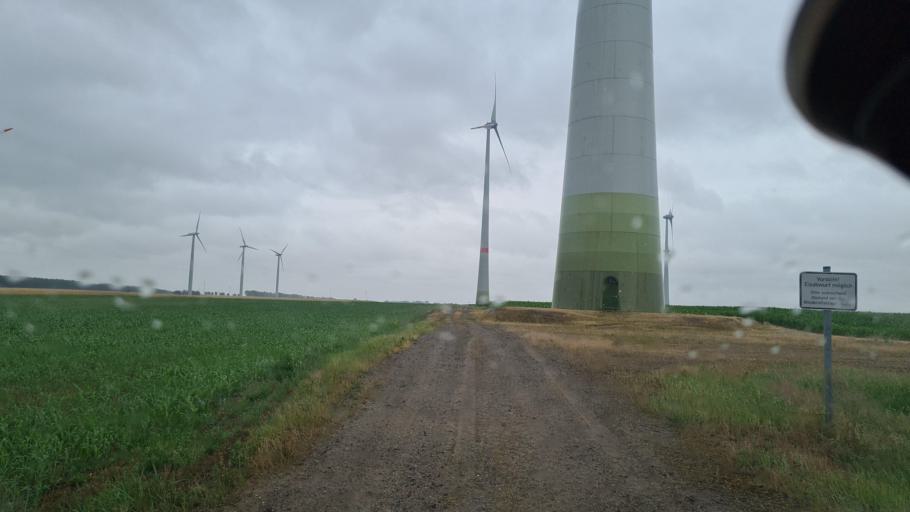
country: DE
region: Brandenburg
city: Juterbog
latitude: 51.9539
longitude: 13.1733
